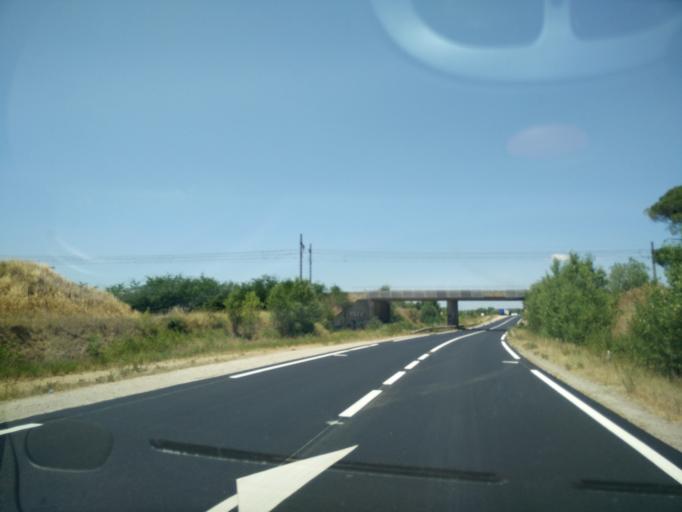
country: FR
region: Languedoc-Roussillon
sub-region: Departement de l'Herault
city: Lunel
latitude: 43.6885
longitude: 4.1487
